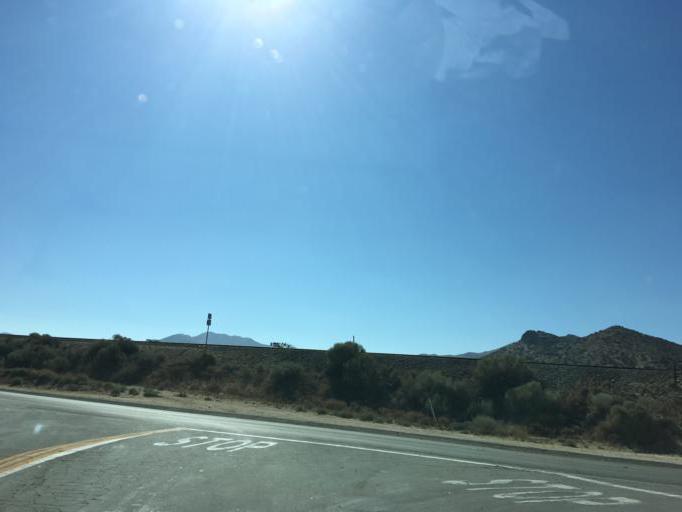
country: US
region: California
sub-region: Los Angeles County
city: Acton
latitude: 34.4699
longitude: -118.1929
